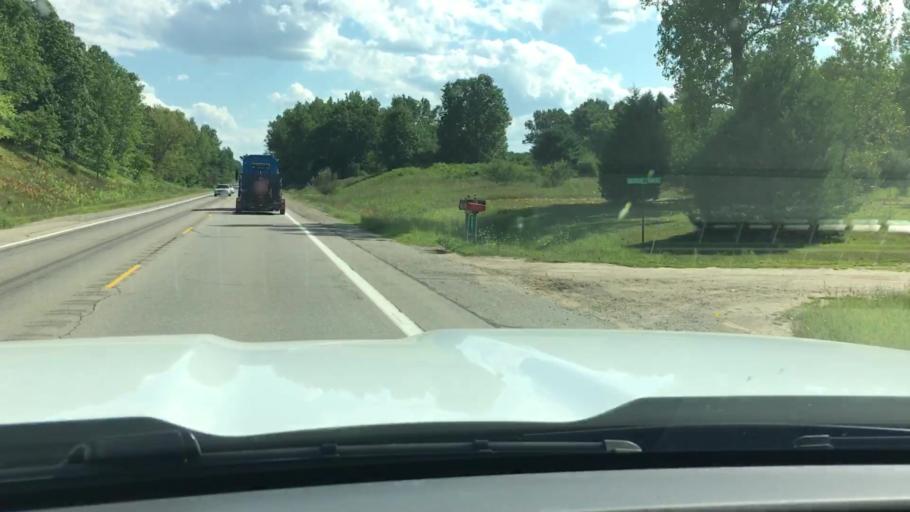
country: US
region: Michigan
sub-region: Ionia County
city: Ionia
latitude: 43.1181
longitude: -85.0751
